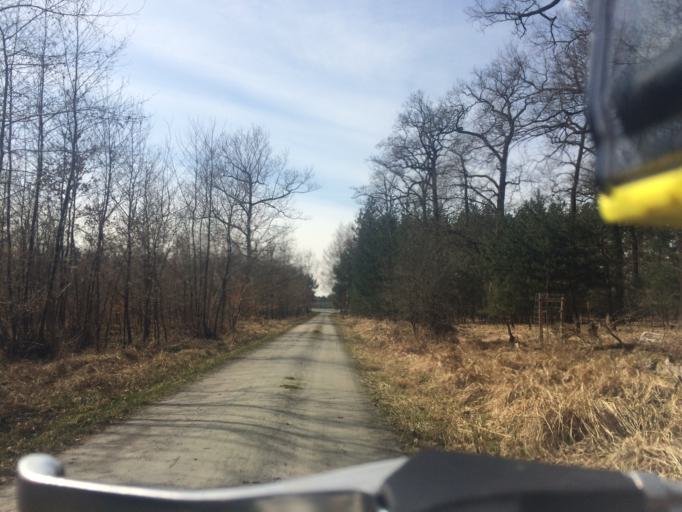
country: DE
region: Hesse
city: Morfelden-Walldorf
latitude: 49.9994
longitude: 8.5326
